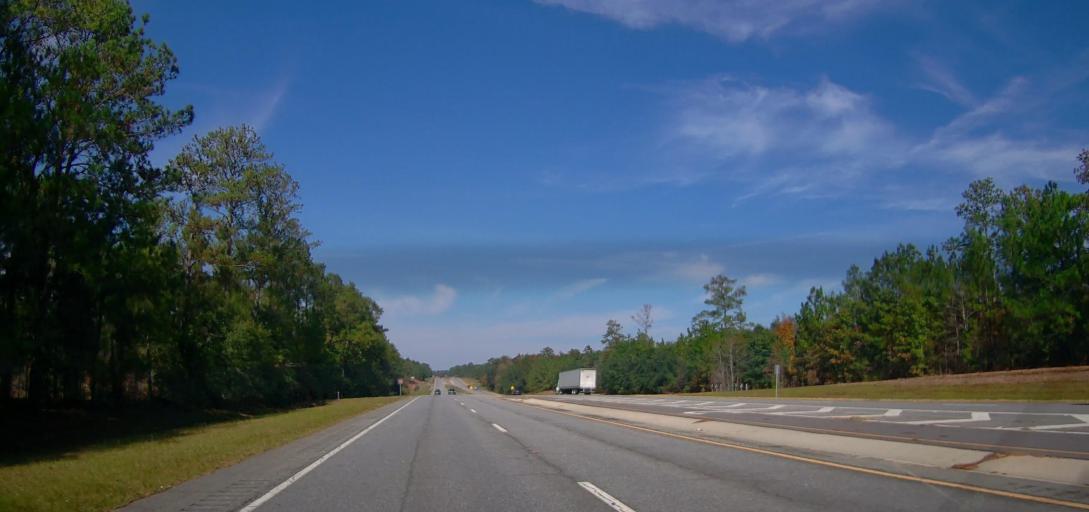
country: US
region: Georgia
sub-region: Lee County
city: Leesburg
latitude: 31.7144
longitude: -83.9892
